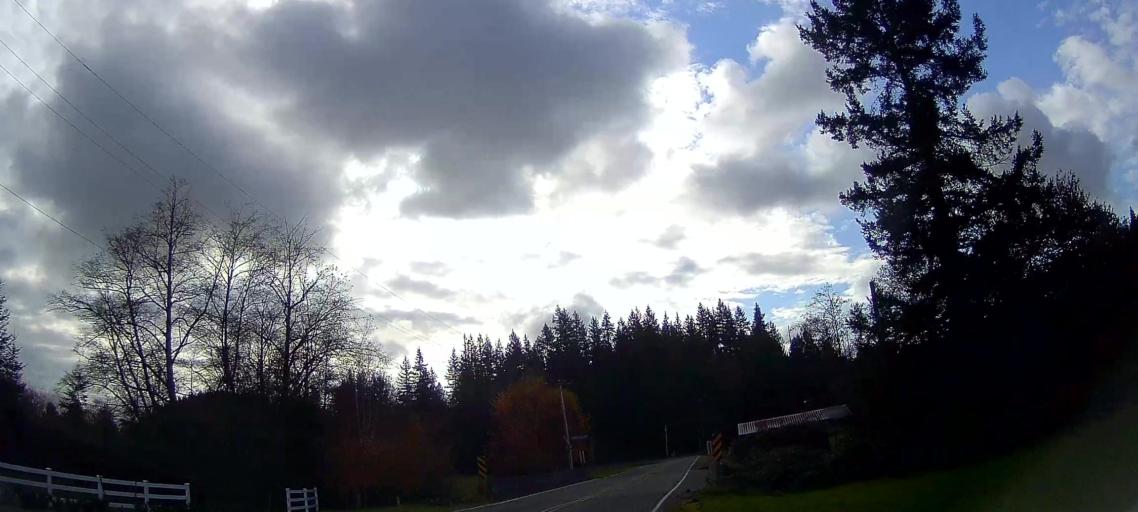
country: US
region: Washington
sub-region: Skagit County
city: Big Lake
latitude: 48.4244
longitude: -122.2098
